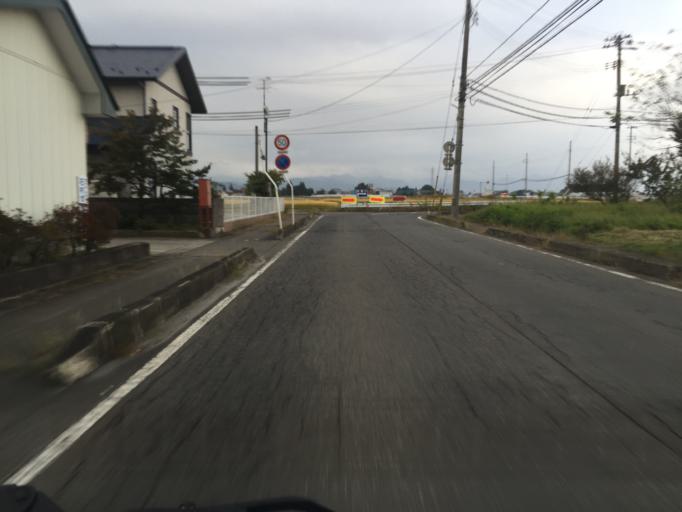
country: JP
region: Fukushima
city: Kitakata
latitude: 37.5107
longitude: 139.8775
